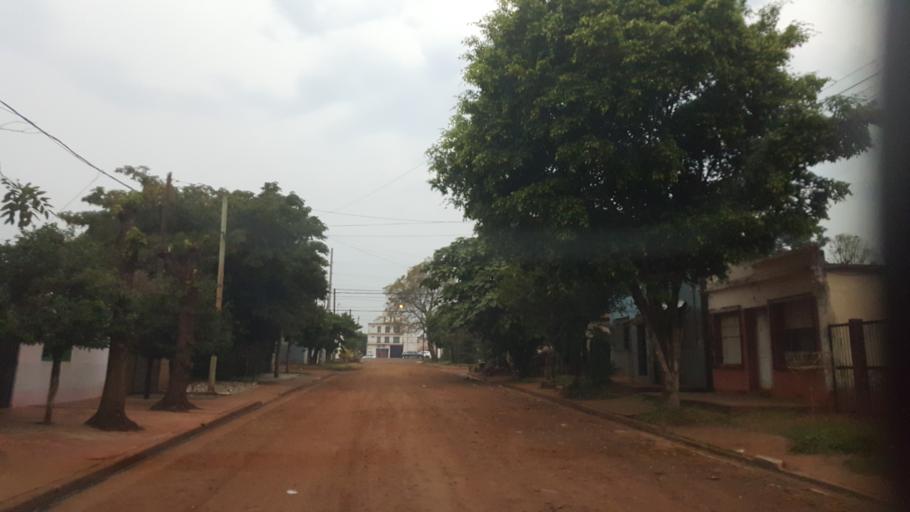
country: AR
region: Misiones
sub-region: Departamento de Capital
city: Posadas
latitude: -27.4000
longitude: -55.9296
